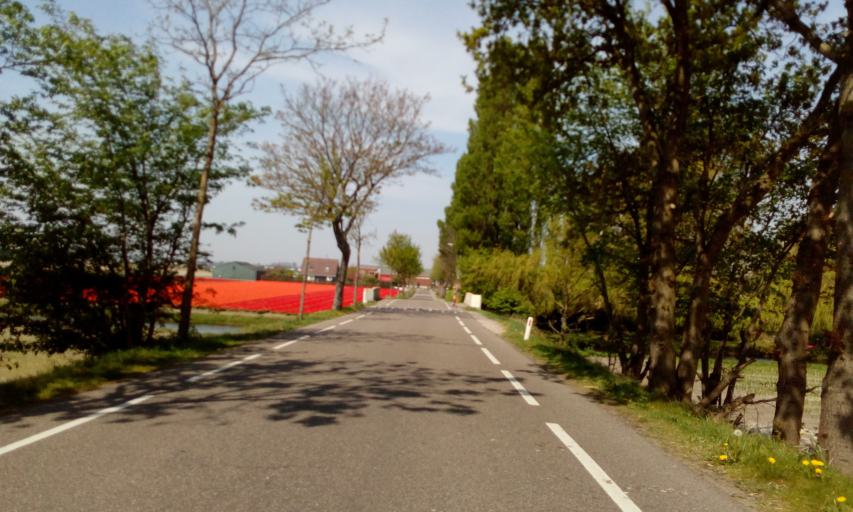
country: NL
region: South Holland
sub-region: Gemeente Hillegom
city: Hillegom
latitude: 52.2882
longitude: 4.5644
